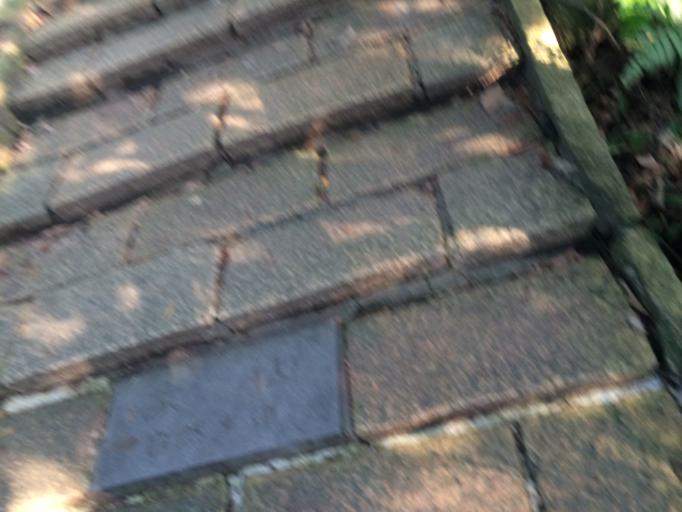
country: TW
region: Taipei
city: Taipei
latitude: 25.0274
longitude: 121.5716
